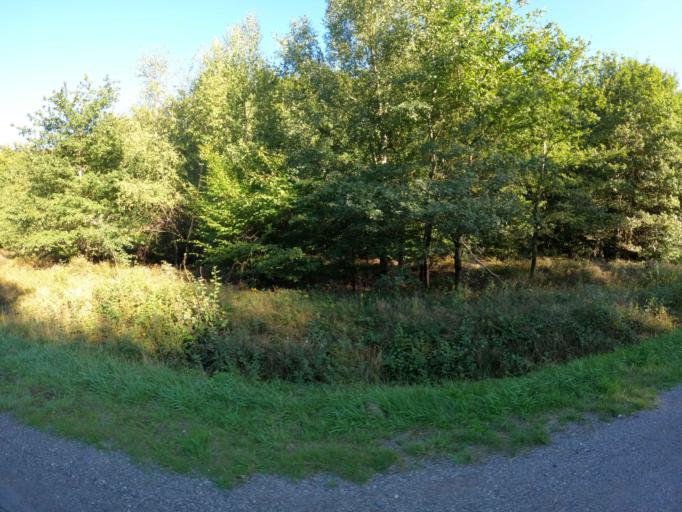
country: FR
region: Bourgogne
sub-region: Departement de Saone-et-Loire
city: Blanzy
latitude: 46.7125
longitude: 4.4222
